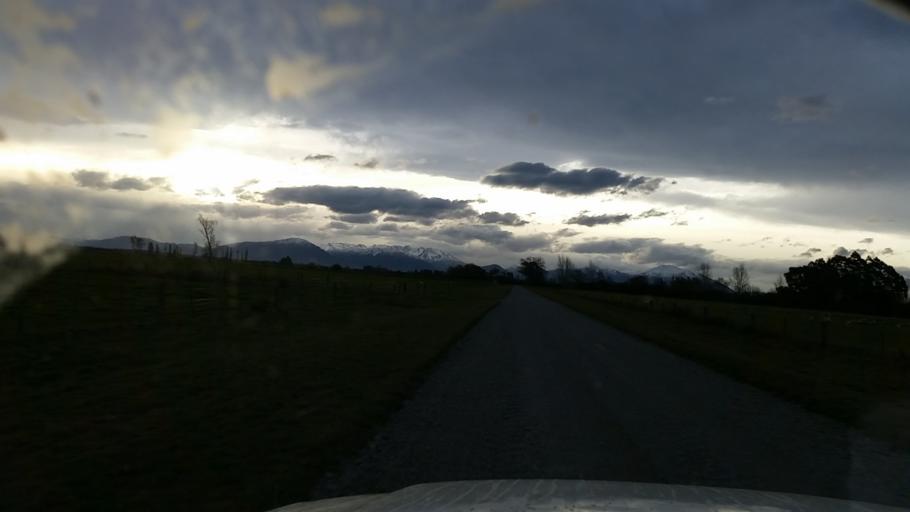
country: NZ
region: Canterbury
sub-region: Ashburton District
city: Ashburton
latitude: -43.8414
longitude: 171.6577
